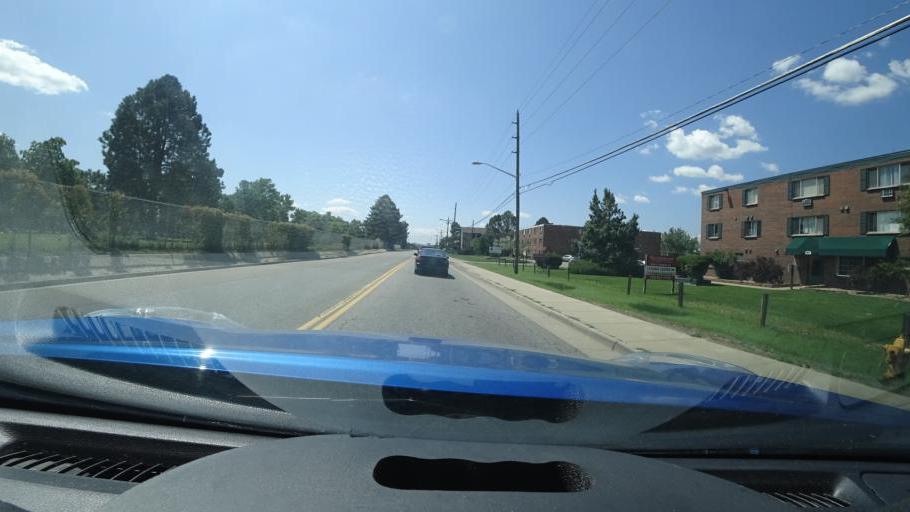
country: US
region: Colorado
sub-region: Arapahoe County
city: Glendale
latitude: 39.7023
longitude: -104.9035
